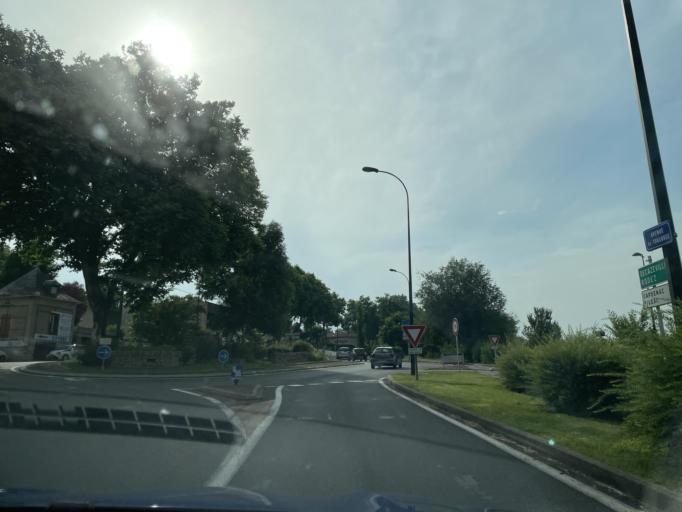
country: FR
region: Midi-Pyrenees
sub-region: Departement de l'Aveyron
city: Villefranche-de-Rouergue
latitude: 44.3590
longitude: 2.0216
